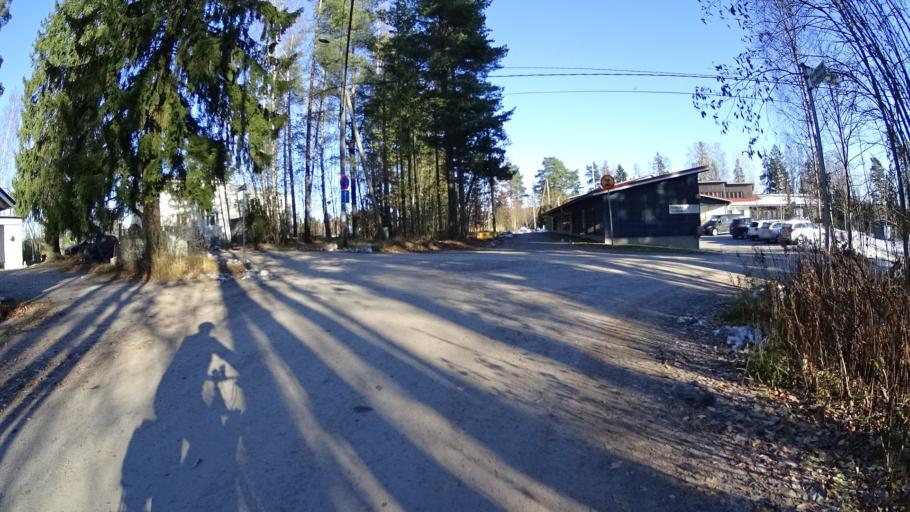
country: FI
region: Uusimaa
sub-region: Helsinki
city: Kauniainen
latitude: 60.2235
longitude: 24.7371
